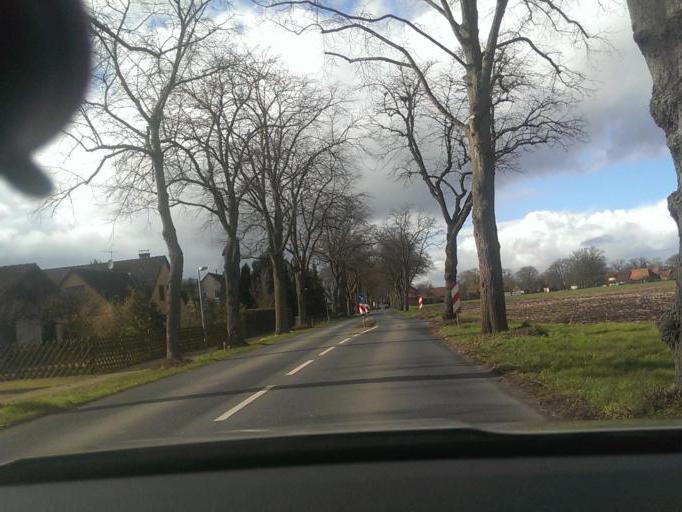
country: DE
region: Lower Saxony
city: Elze
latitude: 52.5783
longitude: 9.7432
